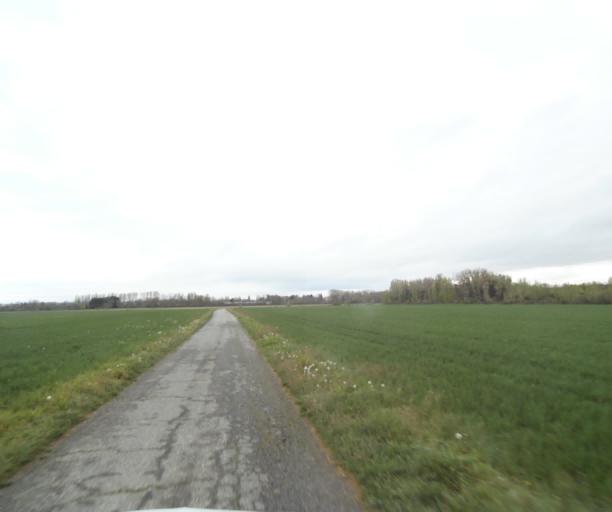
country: FR
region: Midi-Pyrenees
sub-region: Departement de l'Ariege
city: Saverdun
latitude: 43.2207
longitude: 1.5992
